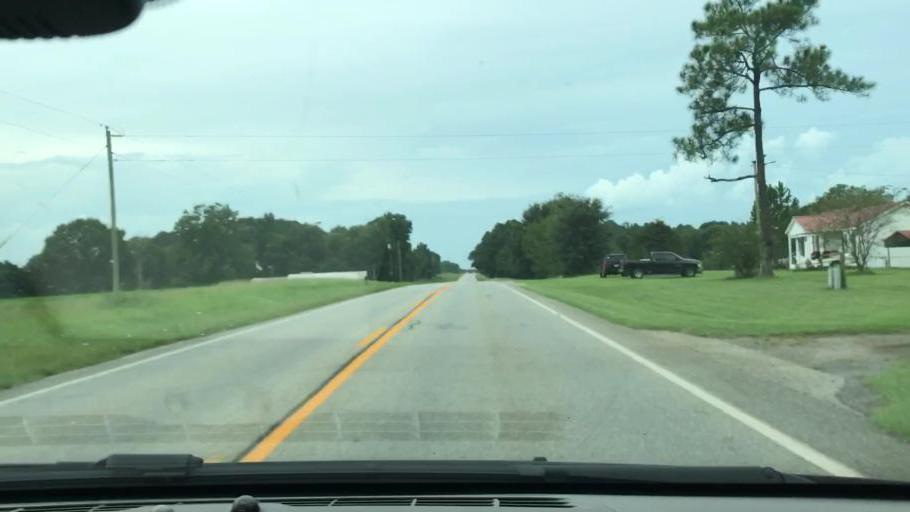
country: US
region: Georgia
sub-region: Early County
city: Blakely
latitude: 31.3468
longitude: -84.9799
